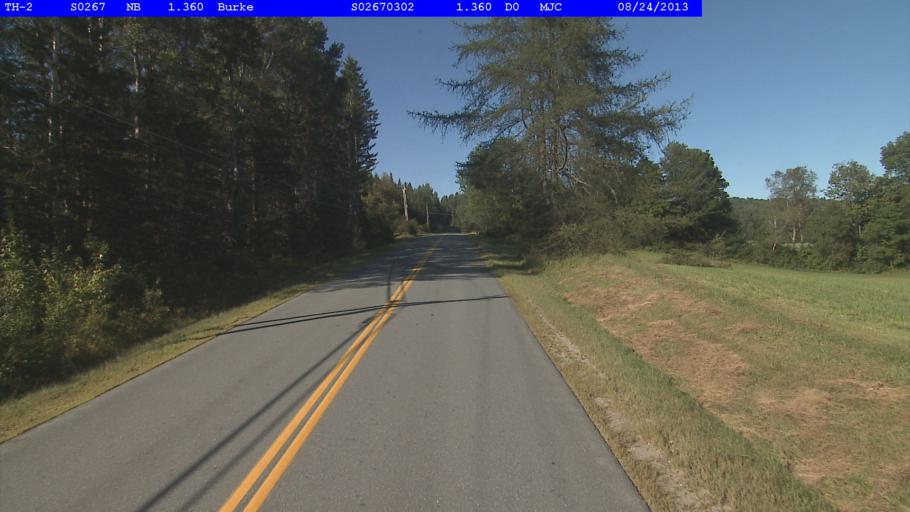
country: US
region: Vermont
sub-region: Caledonia County
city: Lyndonville
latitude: 44.6058
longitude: -71.9380
